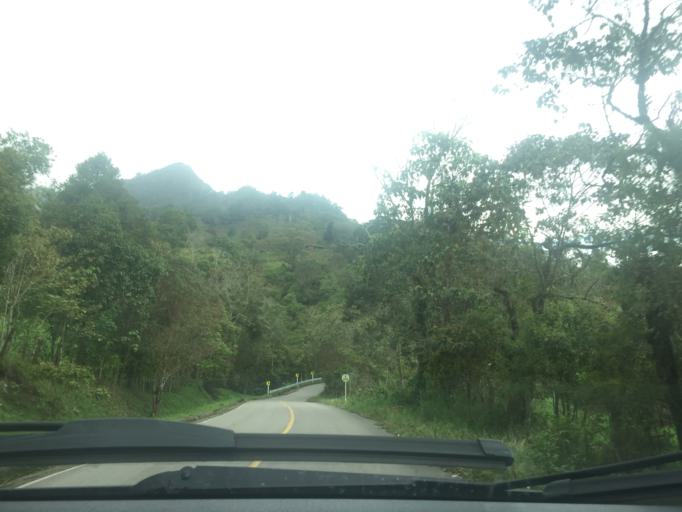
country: CO
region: Cundinamarca
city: Supata
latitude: 5.0418
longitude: -74.2423
